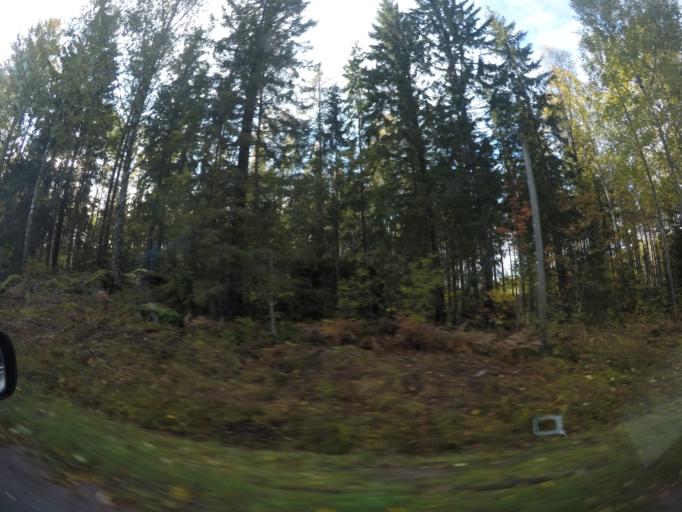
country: SE
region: Soedermanland
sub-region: Eskilstuna Kommun
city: Kvicksund
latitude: 59.3609
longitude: 16.2643
